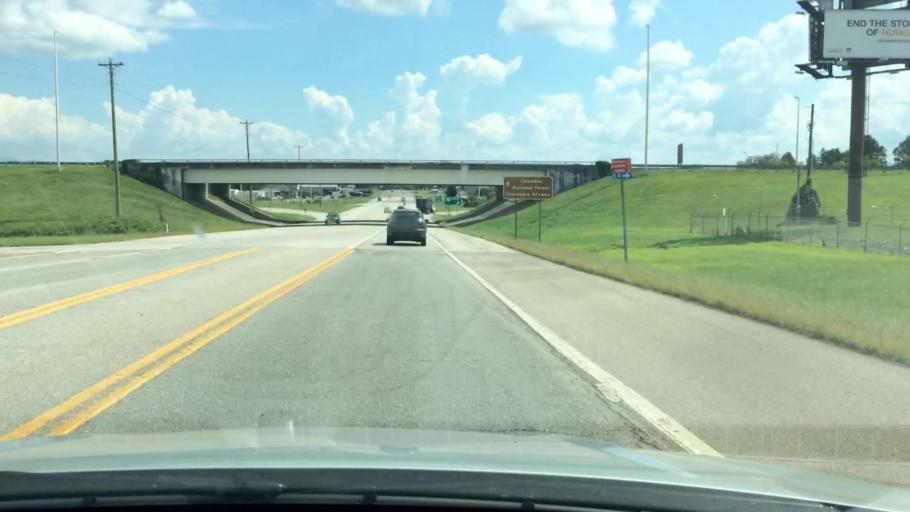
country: US
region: Tennessee
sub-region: Monroe County
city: Madisonville
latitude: 35.5104
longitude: -84.3724
